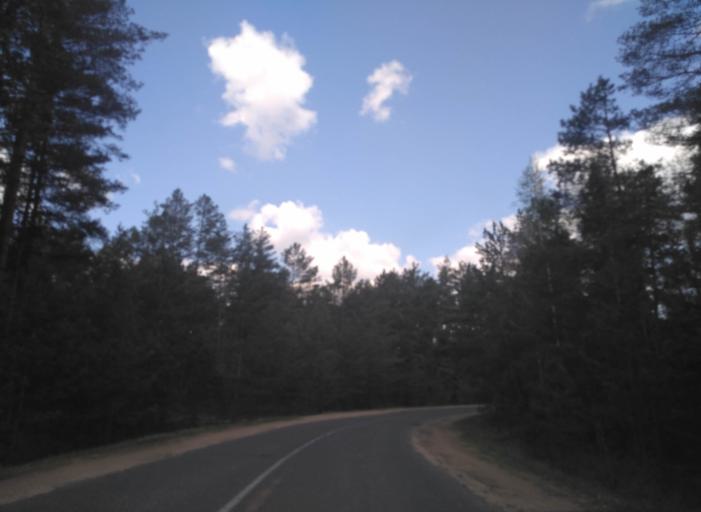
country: BY
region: Minsk
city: Radashkovichy
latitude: 54.1716
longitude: 27.2440
